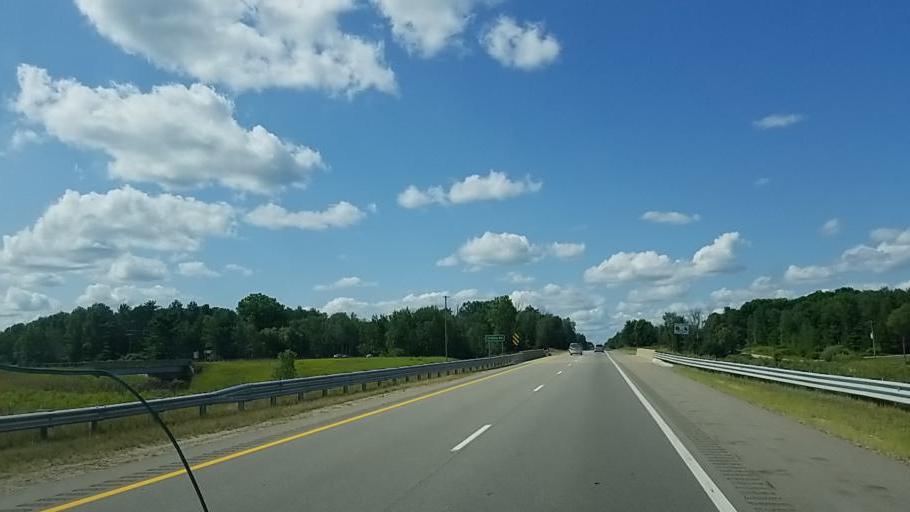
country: US
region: Michigan
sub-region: Mecosta County
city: Big Rapids
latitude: 43.6266
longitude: -85.5010
